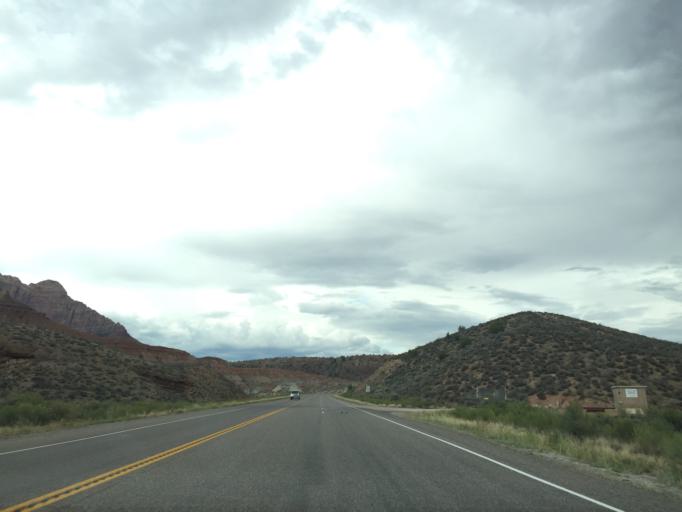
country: US
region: Utah
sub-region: Washington County
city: LaVerkin
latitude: 37.1704
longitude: -113.0752
